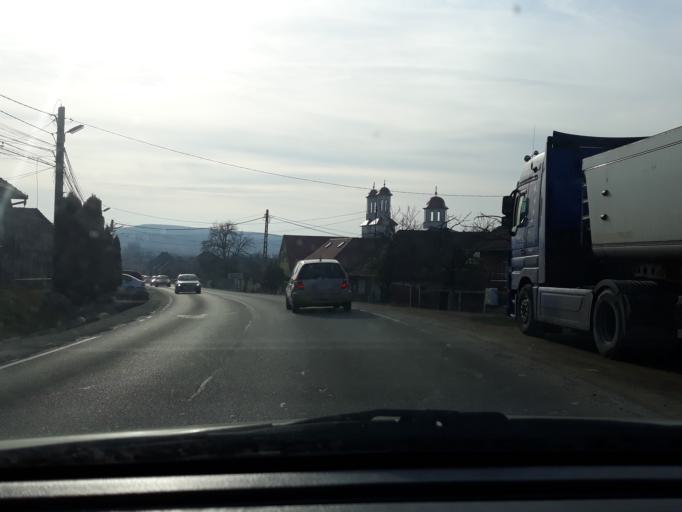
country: RO
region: Salaj
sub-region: Comuna Criseni
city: Criseni
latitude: 47.2325
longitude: 23.0465
